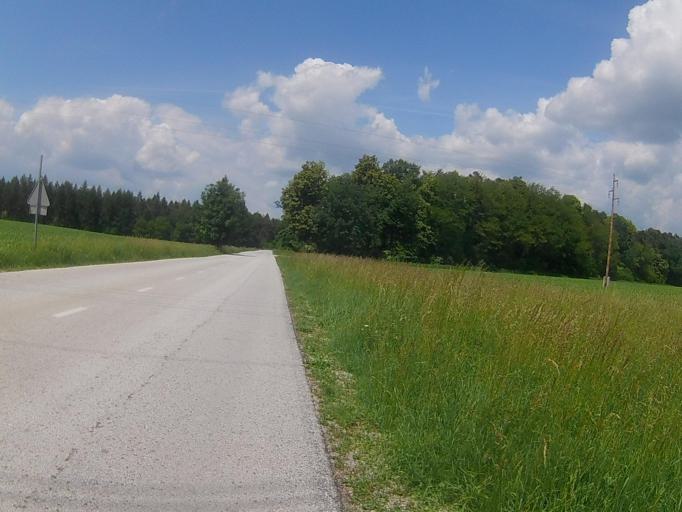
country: SI
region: Kidricevo
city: Kidricevo
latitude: 46.4316
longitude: 15.7793
